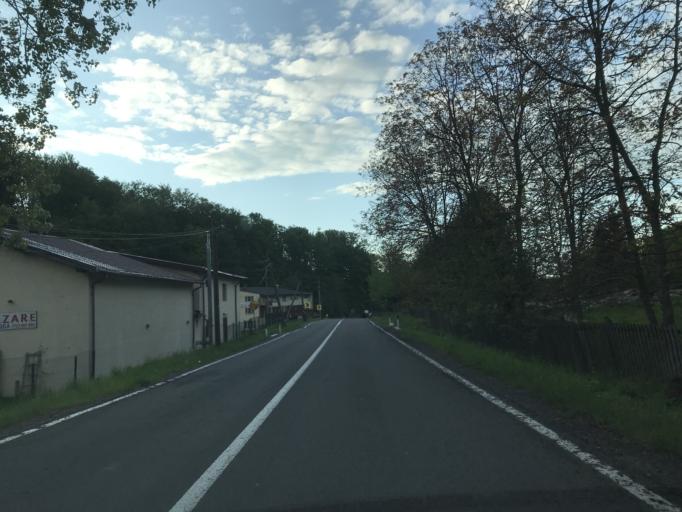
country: RO
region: Sibiu
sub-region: Comuna Cartisoara
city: Cartisoara
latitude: 45.6838
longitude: 24.5750
